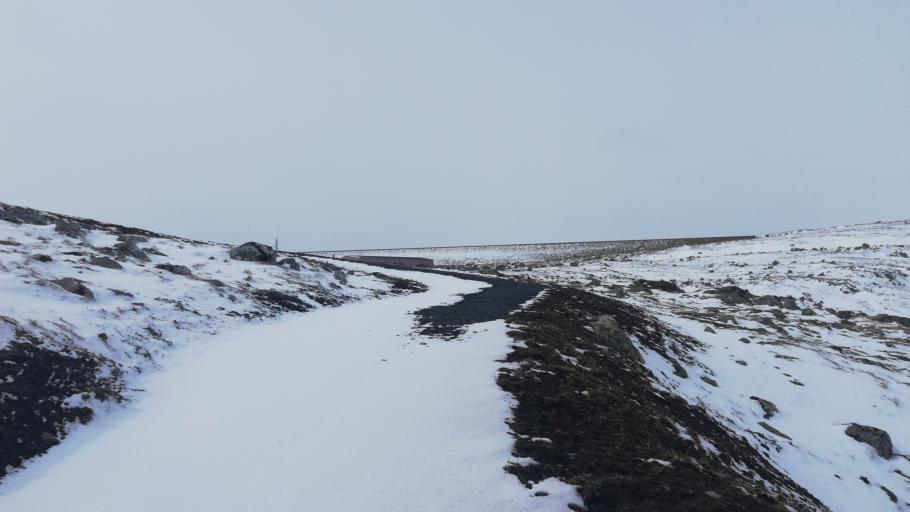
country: FO
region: Streymoy
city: Hoyvik
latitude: 62.0306
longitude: -6.8089
